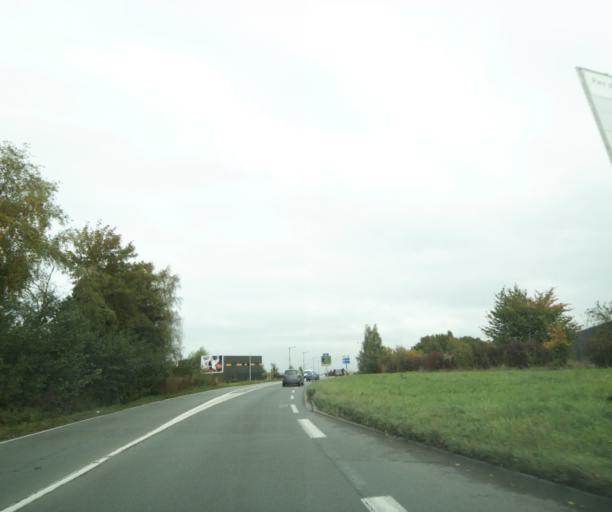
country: FR
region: Nord-Pas-de-Calais
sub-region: Departement du Nord
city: Lesquin
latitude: 50.5827
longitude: 3.1376
